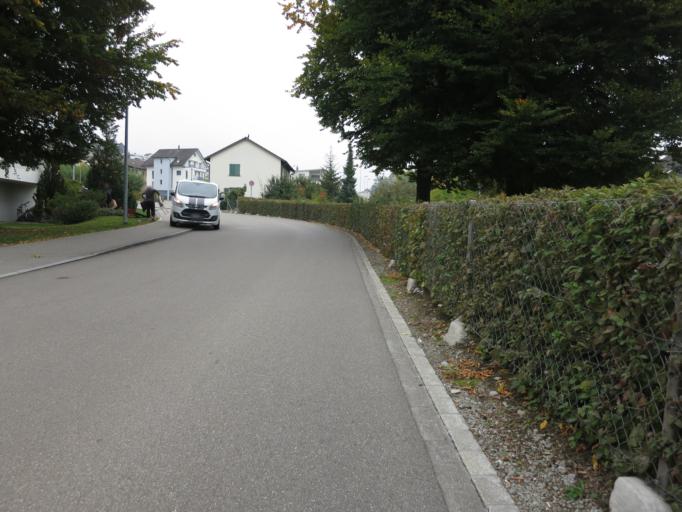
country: CH
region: Saint Gallen
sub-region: Wahlkreis See-Gaster
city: Rapperswil
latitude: 47.2391
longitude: 8.8219
